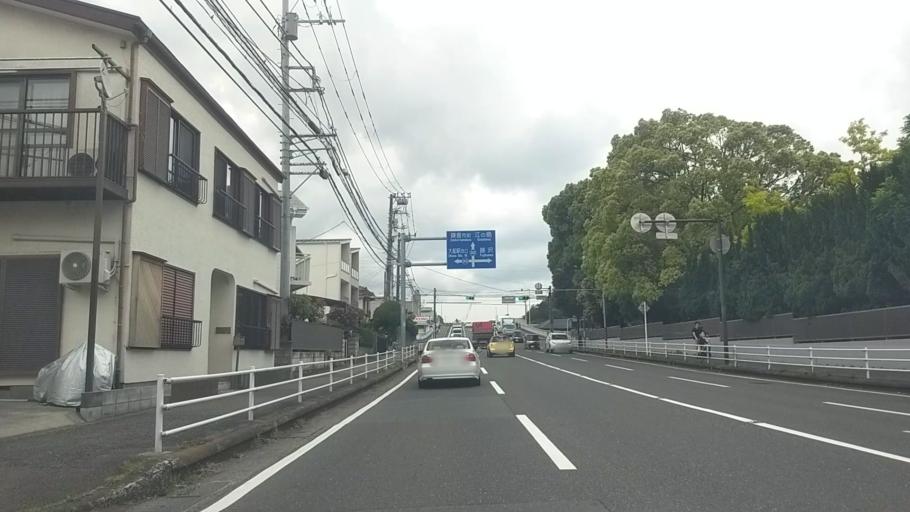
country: JP
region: Kanagawa
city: Kamakura
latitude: 35.3484
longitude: 139.5219
